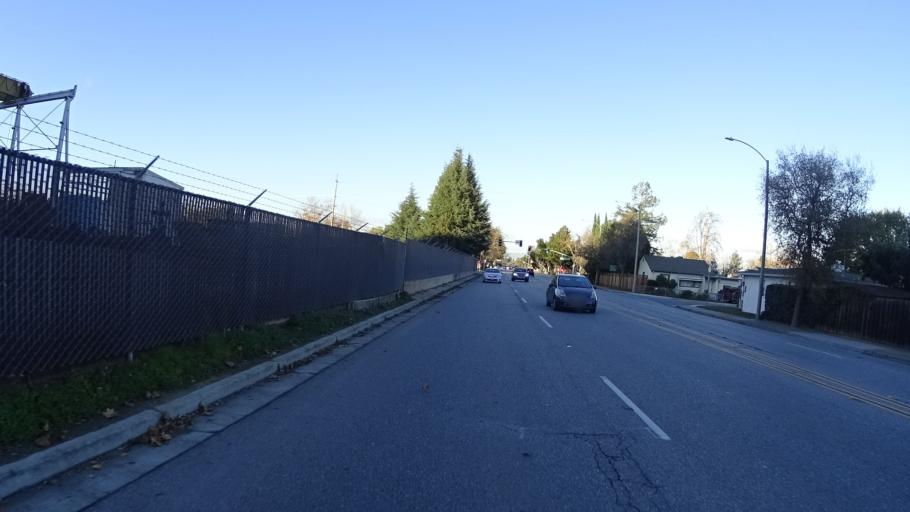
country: US
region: California
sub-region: Santa Clara County
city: Sunnyvale
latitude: 37.3787
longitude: -122.0195
